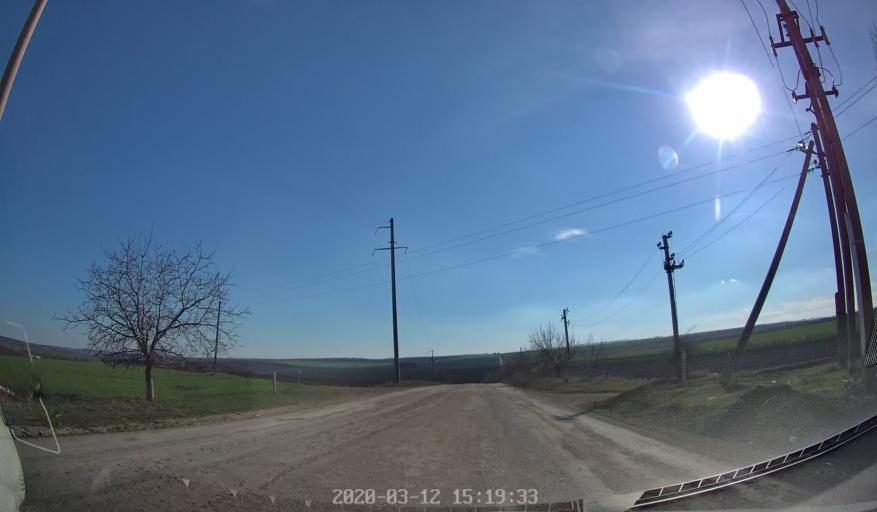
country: MD
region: Chisinau
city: Ciorescu
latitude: 47.2127
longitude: 28.9294
